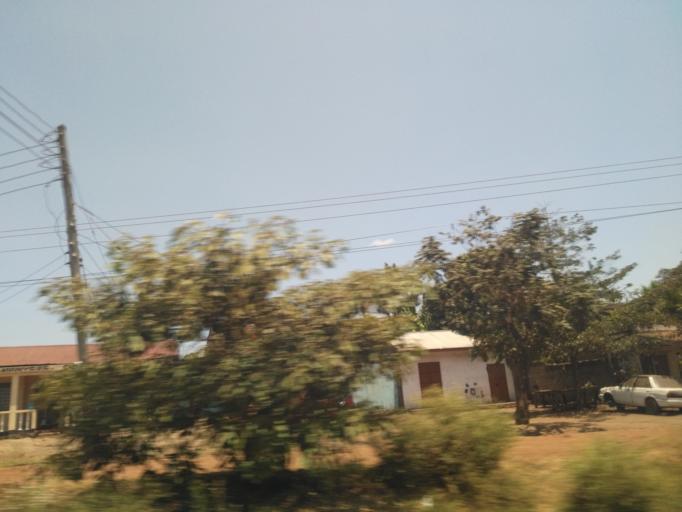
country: TZ
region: Arusha
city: Arusha
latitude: -3.3704
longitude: 36.6753
